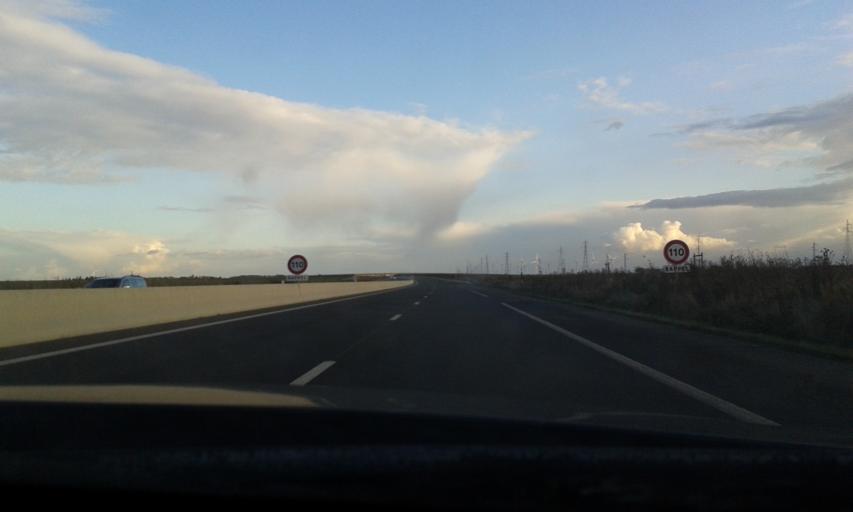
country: FR
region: Centre
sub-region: Departement d'Eure-et-Loir
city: Sours
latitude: 48.3635
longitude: 1.5996
